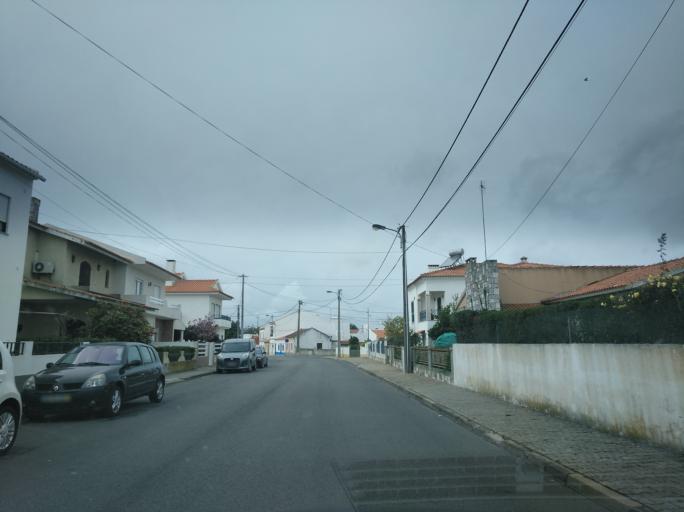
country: PT
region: Setubal
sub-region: Grandola
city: Grandola
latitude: 38.1787
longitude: -8.5701
